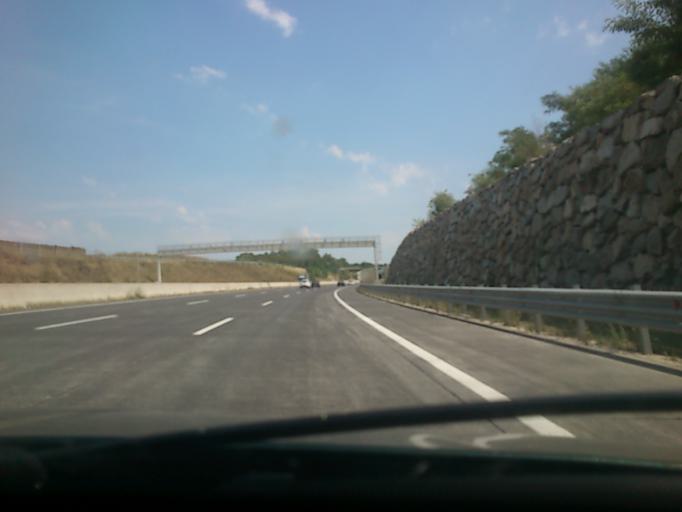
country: AT
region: Lower Austria
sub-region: Politischer Bezirk Mistelbach
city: Wolkersdorf im Weinviertel
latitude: 48.3953
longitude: 16.5103
